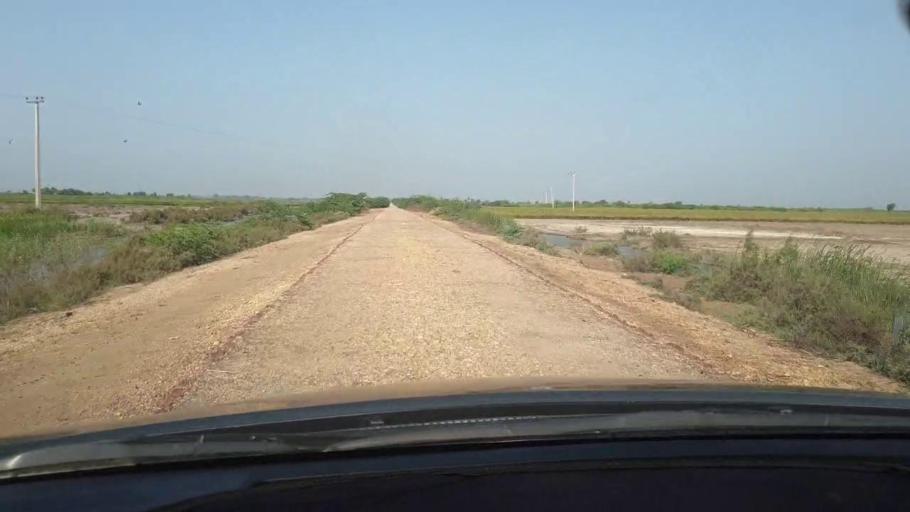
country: PK
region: Sindh
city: Tando Bago
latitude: 24.6799
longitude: 69.1663
